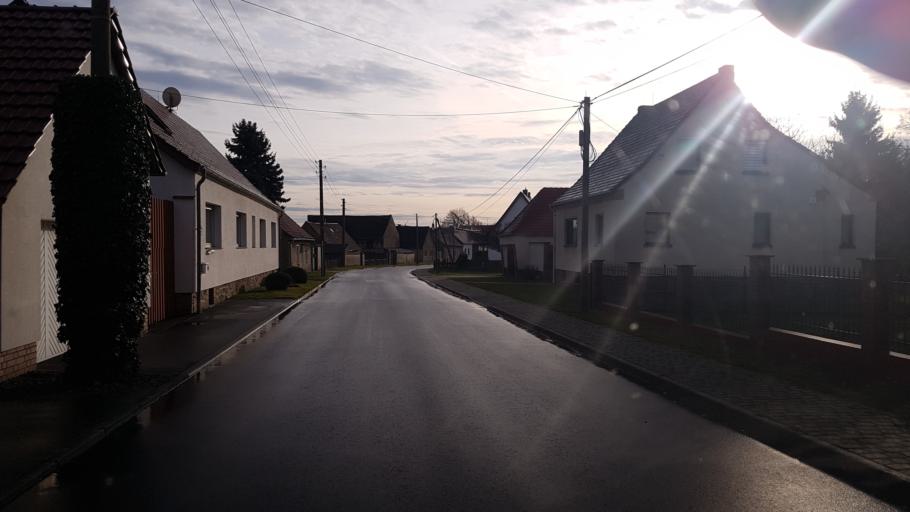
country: DE
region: Brandenburg
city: Hohenbucko
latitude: 51.7401
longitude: 13.4393
